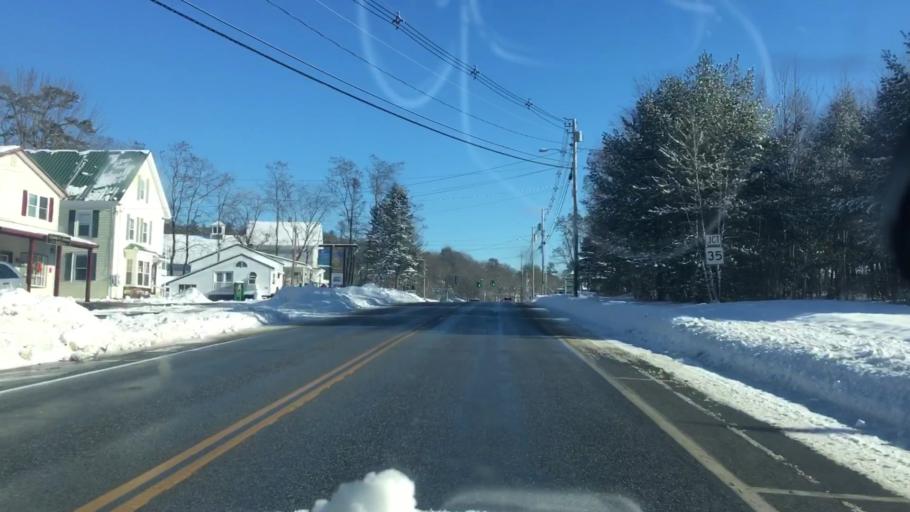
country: US
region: Maine
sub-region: Cumberland County
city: Raymond
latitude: 43.9699
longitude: -70.5964
